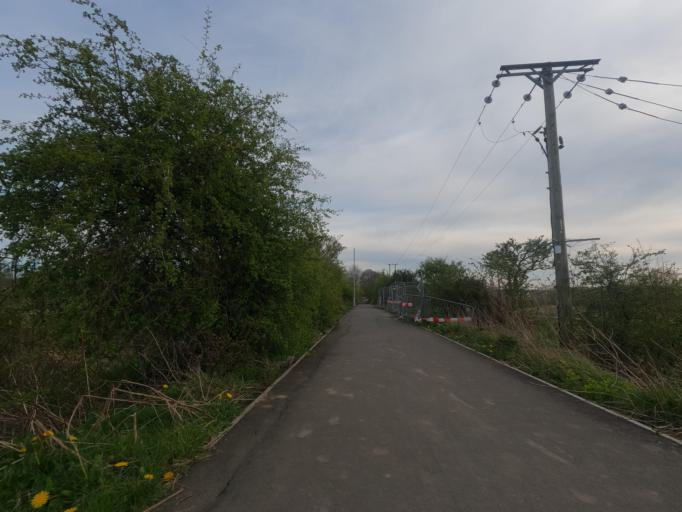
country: GB
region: England
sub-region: Newcastle upon Tyne
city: Hazlerigg
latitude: 55.0258
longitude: -1.6566
